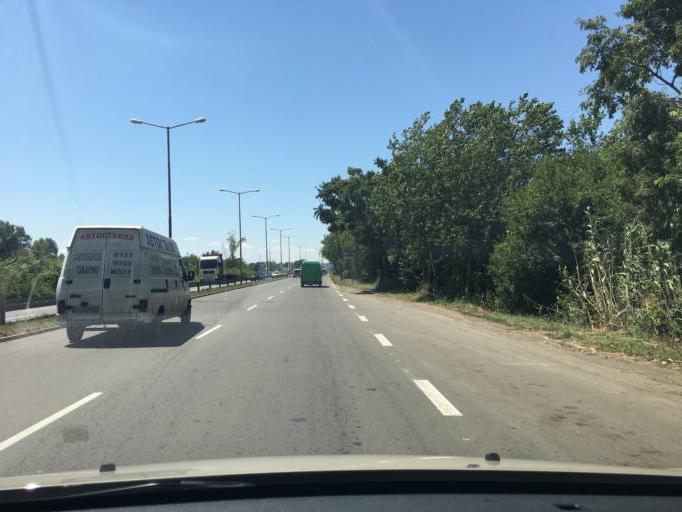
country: BG
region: Burgas
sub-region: Obshtina Burgas
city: Burgas
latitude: 42.4959
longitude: 27.4529
